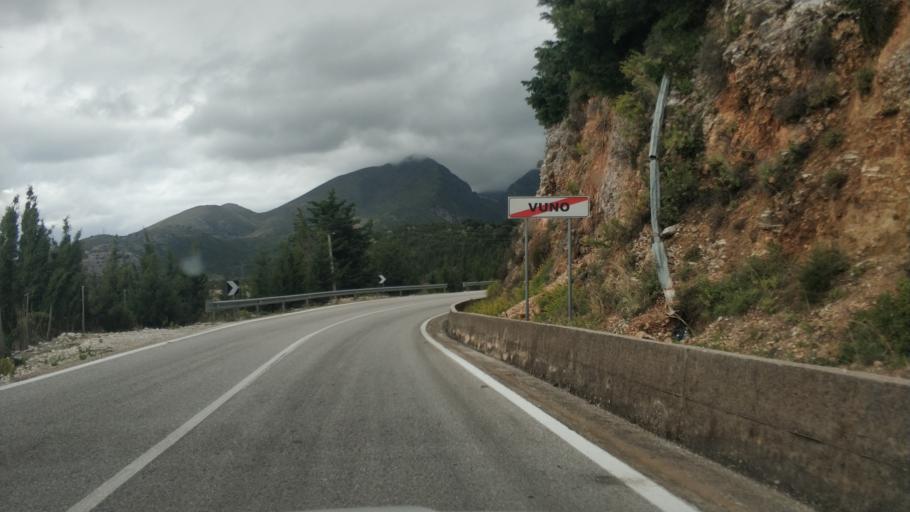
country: AL
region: Vlore
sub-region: Rrethi i Vlores
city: Vranisht
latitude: 40.1412
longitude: 19.6876
